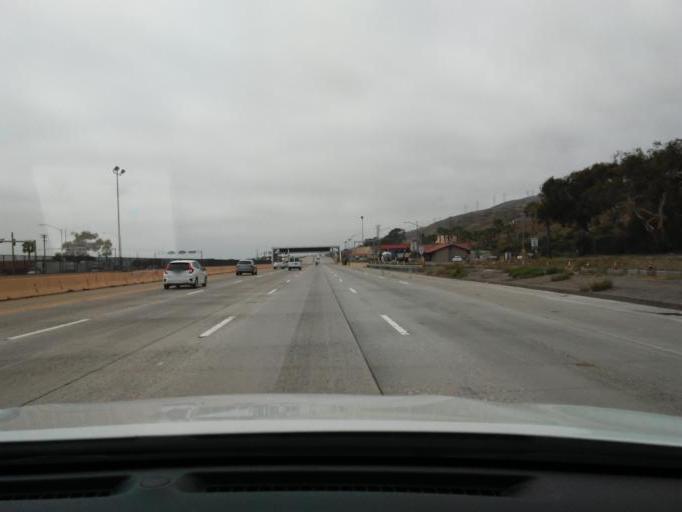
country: US
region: California
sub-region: Orange County
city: San Clemente
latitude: 33.3511
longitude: -117.5229
